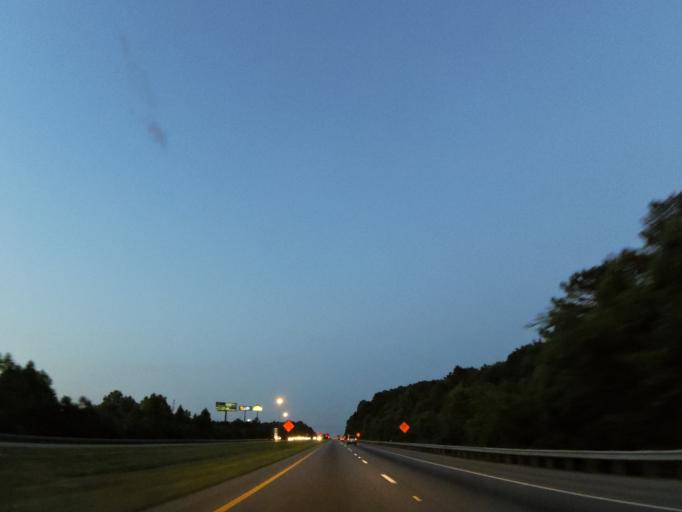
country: US
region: Tennessee
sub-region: Bradley County
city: Cleveland
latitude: 35.1907
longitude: -84.8942
